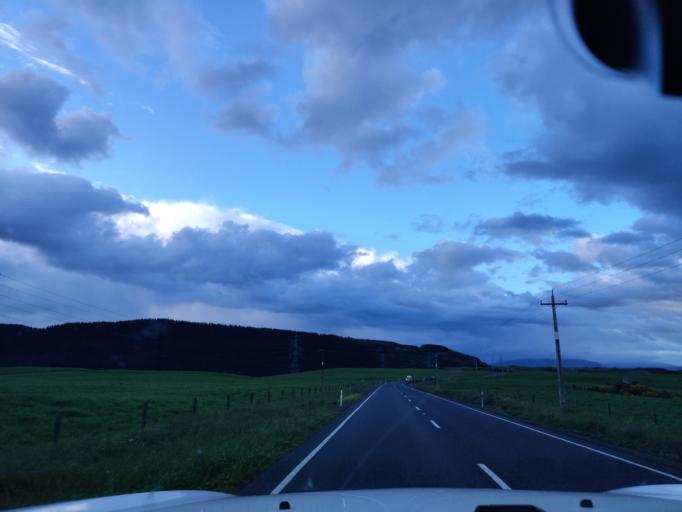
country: NZ
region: Waikato
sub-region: South Waikato District
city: Tokoroa
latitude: -38.3663
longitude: 175.8064
